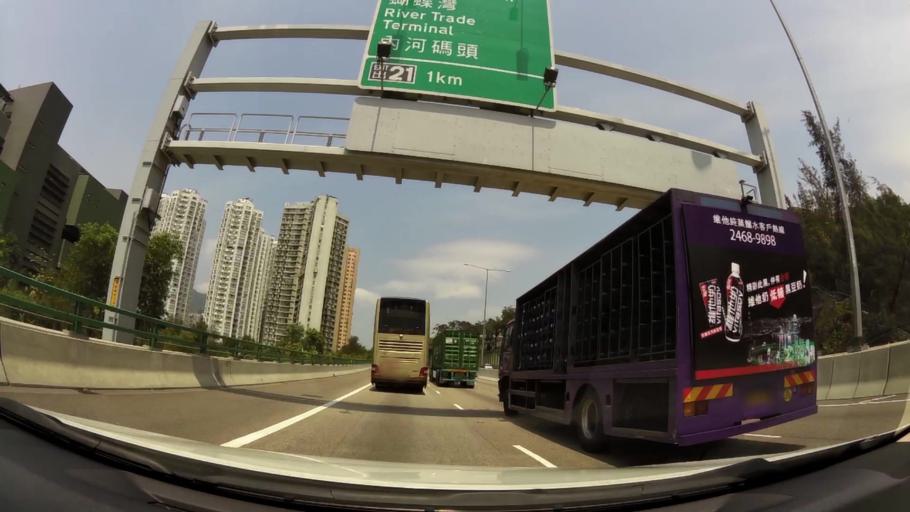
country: HK
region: Tuen Mun
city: Tuen Mun
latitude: 22.3770
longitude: 113.9869
